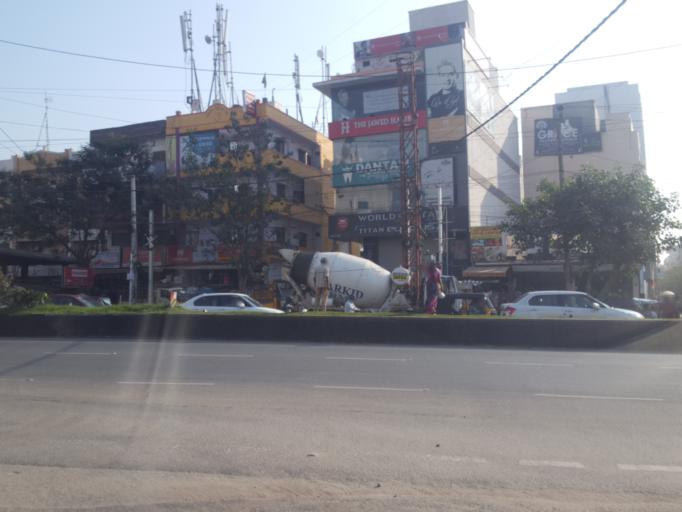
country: IN
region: Telangana
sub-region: Rangareddi
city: Kukatpalli
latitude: 17.4510
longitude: 78.3636
